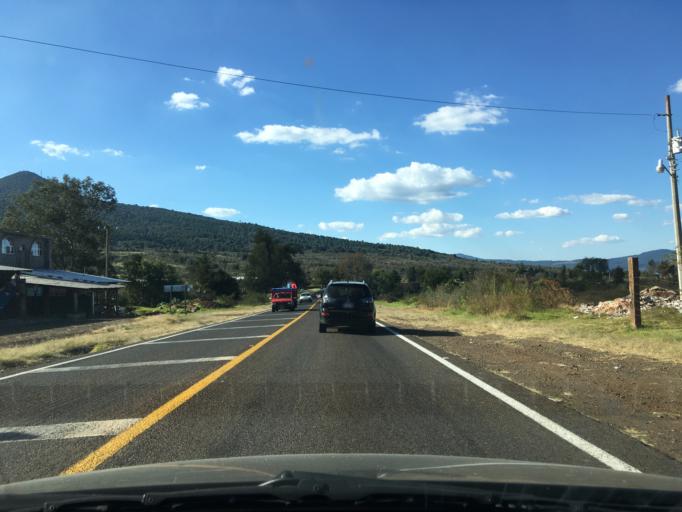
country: MX
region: Michoacan
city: Tzintzuntzan
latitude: 19.6050
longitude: -101.5744
